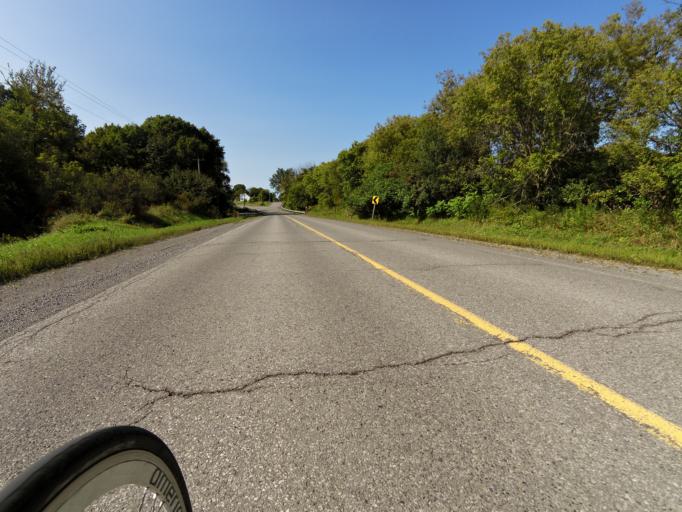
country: CA
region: Ontario
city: Carleton Place
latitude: 45.3547
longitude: -76.1179
